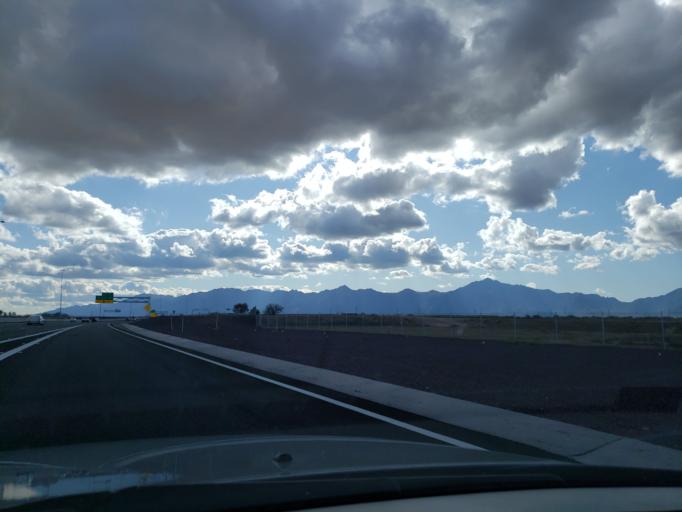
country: US
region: Arizona
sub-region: Maricopa County
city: Laveen
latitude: 33.3729
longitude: -112.1899
